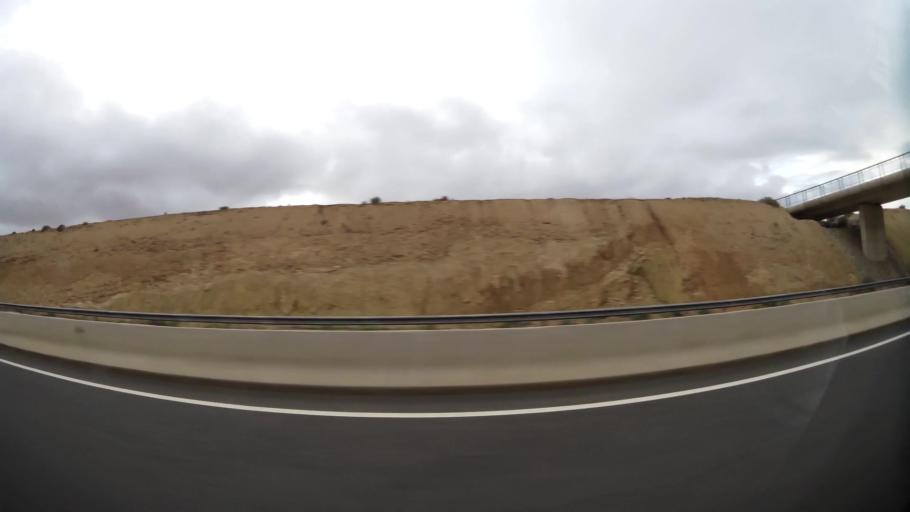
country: MA
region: Taza-Al Hoceima-Taounate
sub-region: Taza
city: Guercif
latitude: 34.3878
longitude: -3.2233
